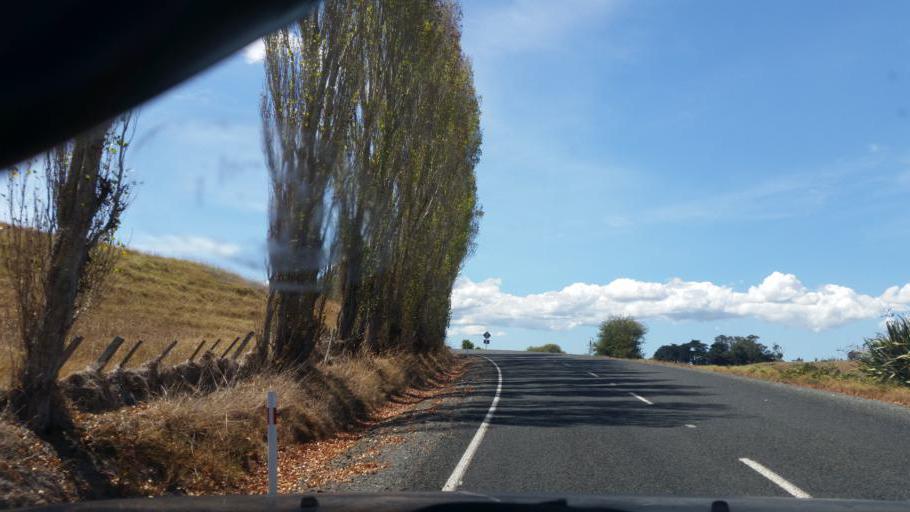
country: NZ
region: Northland
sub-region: Kaipara District
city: Dargaville
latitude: -36.1693
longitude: 174.1653
